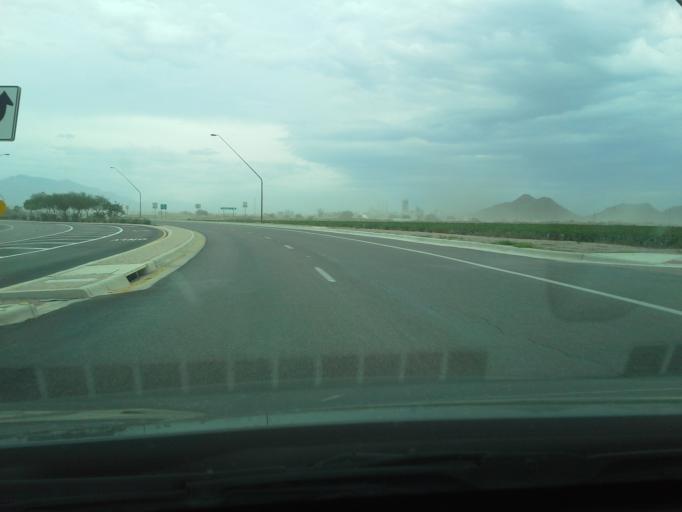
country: US
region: Arizona
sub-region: Pima County
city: Marana
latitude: 32.4229
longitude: -111.1686
